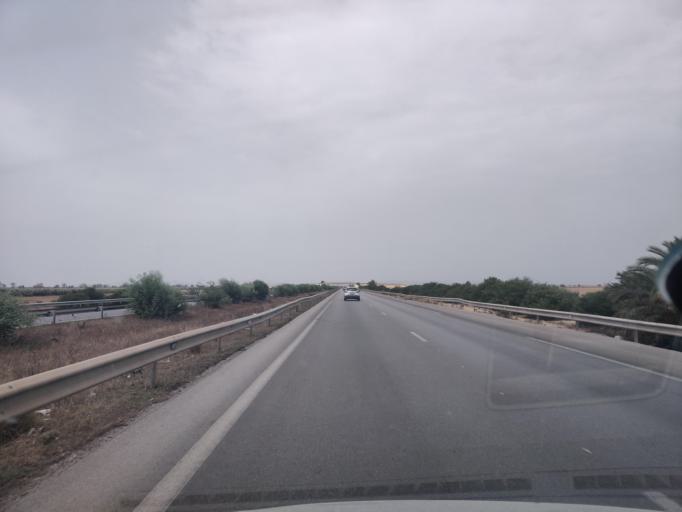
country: TN
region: Susah
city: Harqalah
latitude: 36.0347
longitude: 10.4221
